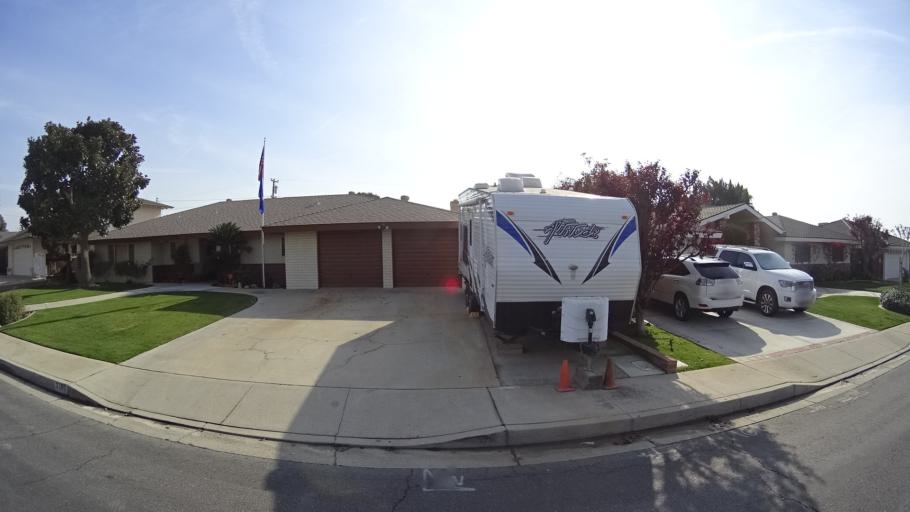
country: US
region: California
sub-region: Kern County
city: Oildale
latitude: 35.4094
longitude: -118.9520
